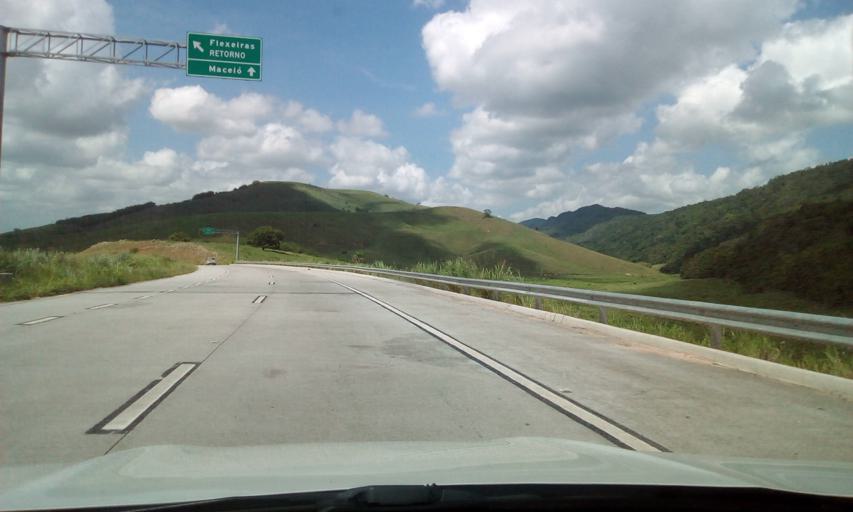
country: BR
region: Alagoas
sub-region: Flexeiras
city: Flexeiras
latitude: -9.2531
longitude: -35.7715
